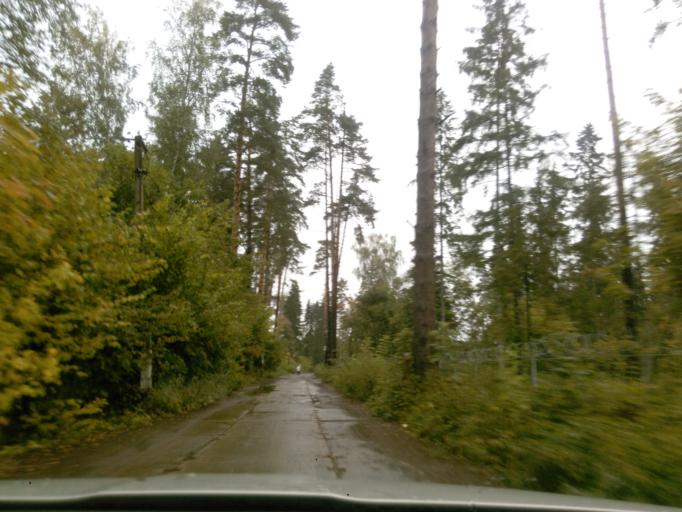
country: RU
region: Moskovskaya
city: Lozhki
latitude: 56.0513
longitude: 37.1010
